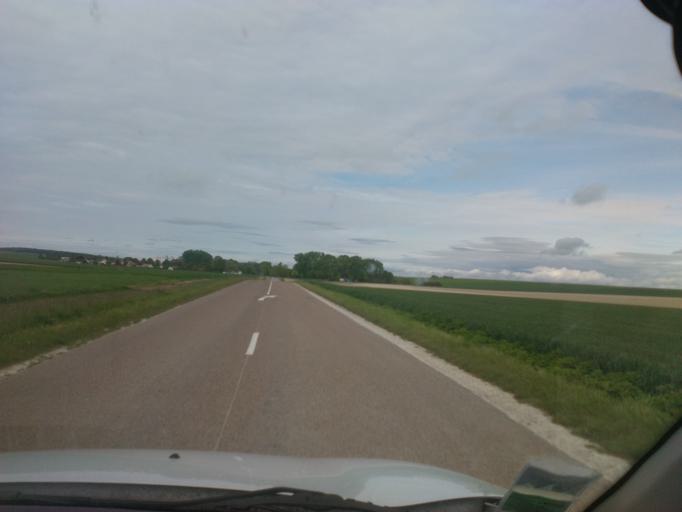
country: FR
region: Champagne-Ardenne
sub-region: Departement de l'Aube
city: Marigny-le-Chatel
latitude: 48.3626
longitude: 3.7198
